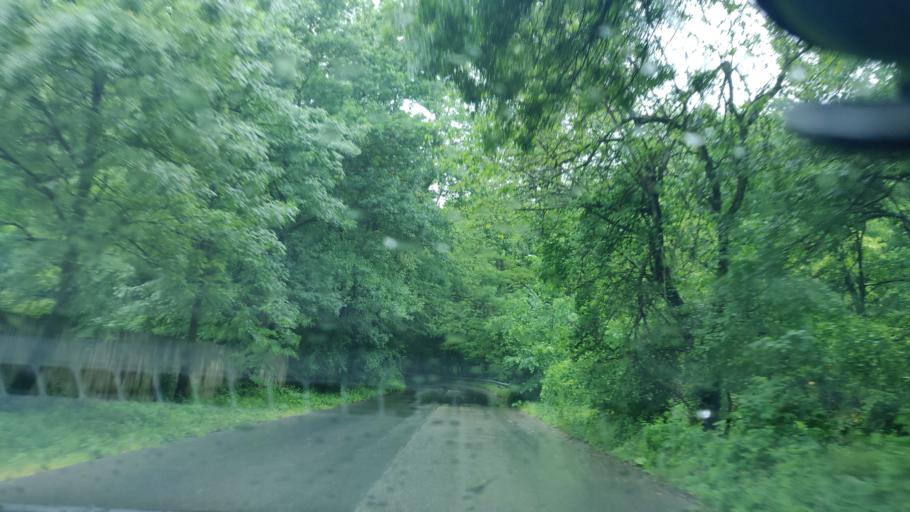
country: RO
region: Giurgiu
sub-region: Comuna Bulbucata
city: Bulbucata
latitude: 44.2884
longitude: 25.7816
